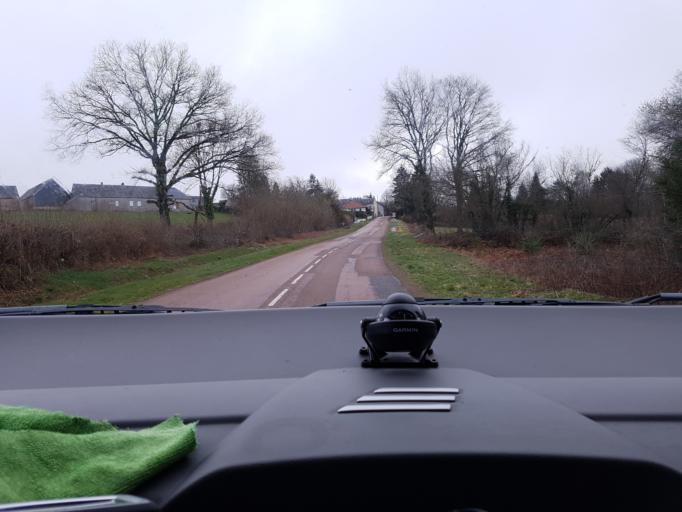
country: FR
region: Bourgogne
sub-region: Departement de la Cote-d'Or
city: Saulieu
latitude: 47.2727
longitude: 4.0288
